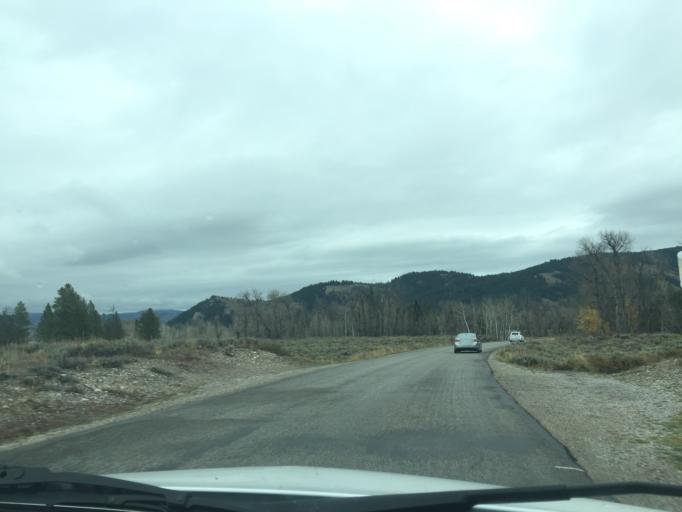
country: US
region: Wyoming
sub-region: Teton County
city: Moose Wilson Road
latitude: 43.6598
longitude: -110.7259
